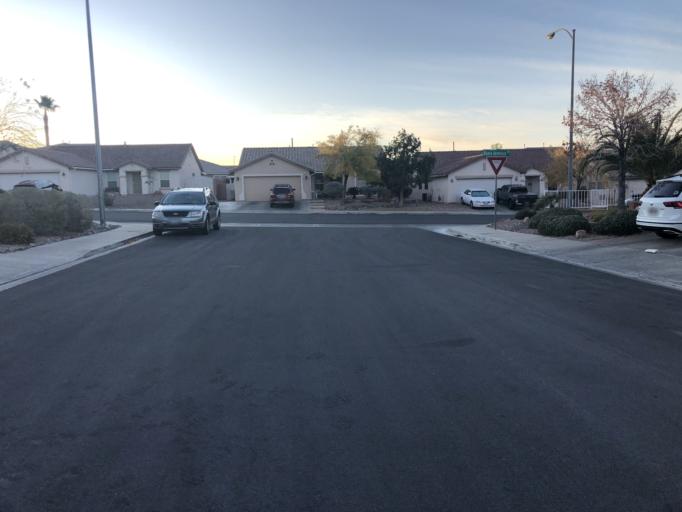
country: US
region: Nevada
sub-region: Clark County
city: Whitney
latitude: 36.0172
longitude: -115.0454
